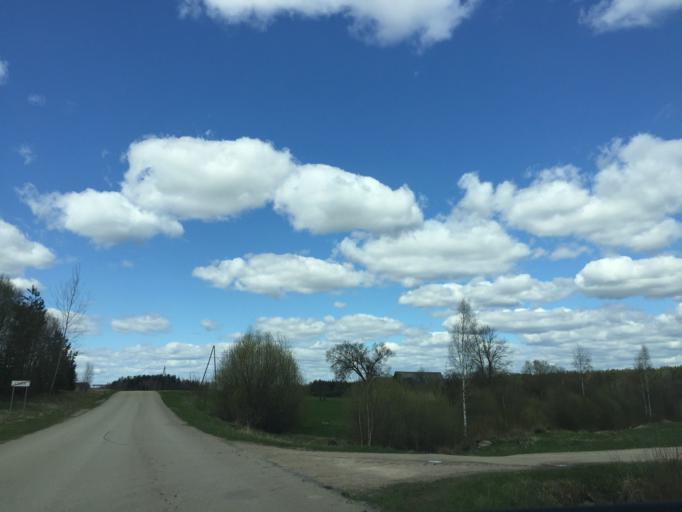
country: LV
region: Rezekne
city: Rezekne
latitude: 56.5678
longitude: 27.1388
